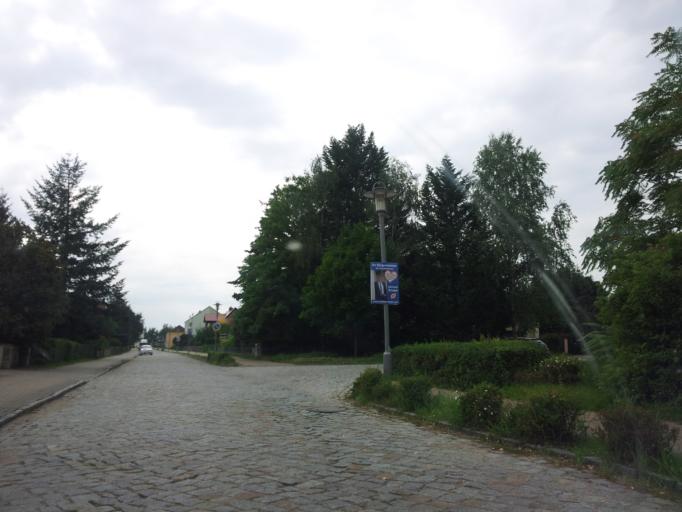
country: DE
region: Brandenburg
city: Treuenbrietzen
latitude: 52.0907
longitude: 12.8546
